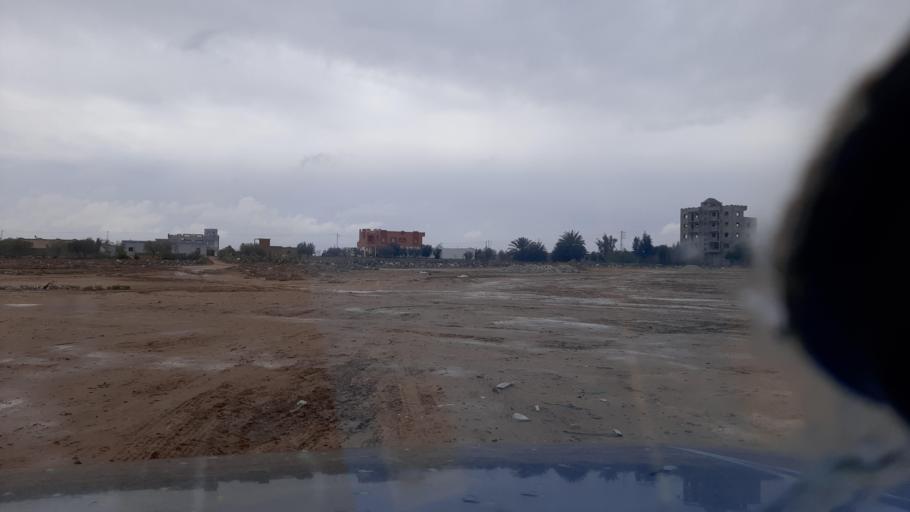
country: TN
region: Al Mahdiyah
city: Shurban
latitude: 35.4353
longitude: 10.3966
